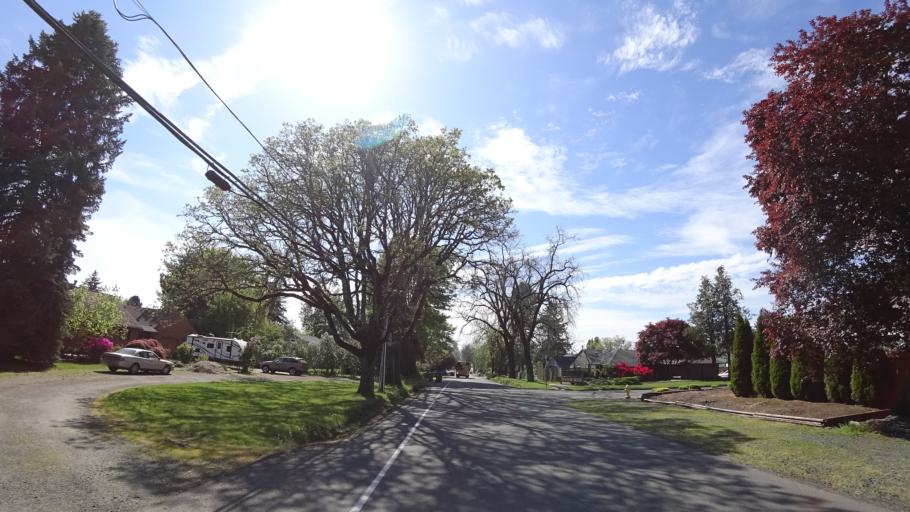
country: US
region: Oregon
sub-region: Washington County
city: Aloha
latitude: 45.5005
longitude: -122.8858
